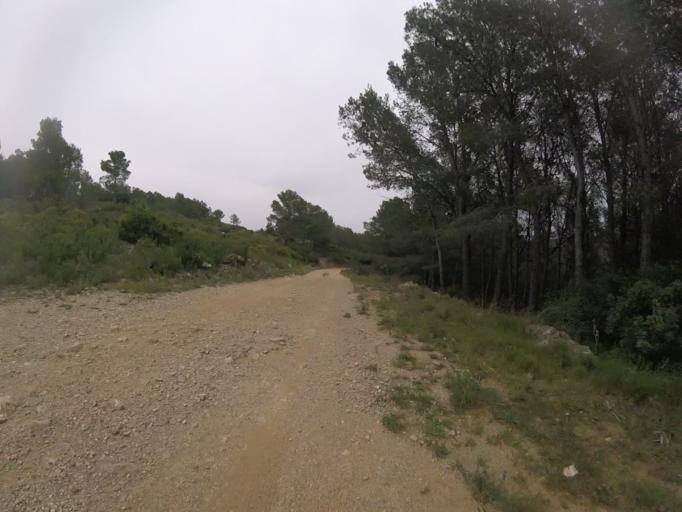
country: ES
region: Valencia
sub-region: Provincia de Castello
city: Alcala de Xivert
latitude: 40.3136
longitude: 0.2665
